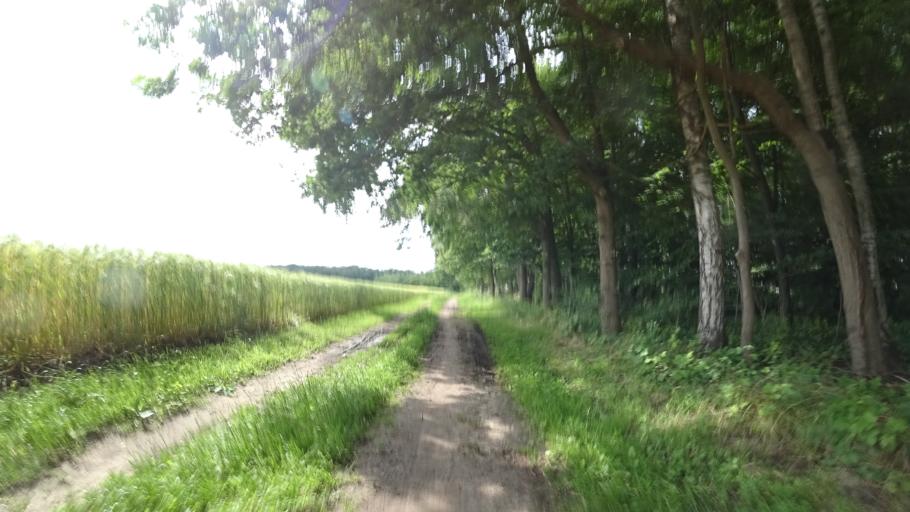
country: DE
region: North Rhine-Westphalia
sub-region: Regierungsbezirk Detmold
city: Guetersloh
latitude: 51.9257
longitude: 8.3785
